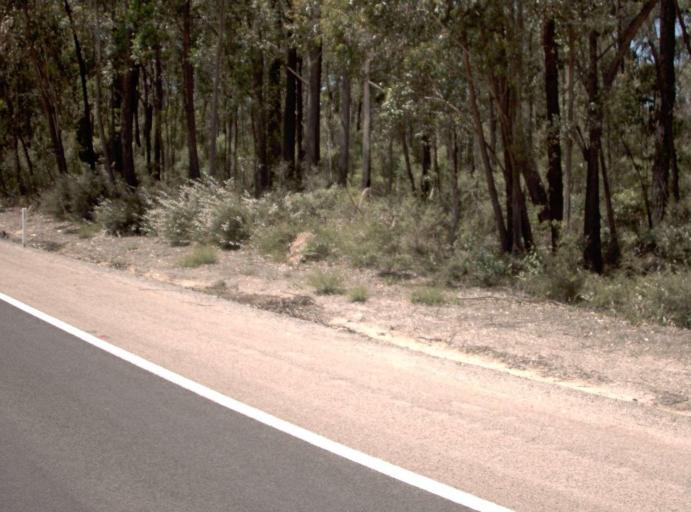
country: AU
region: Victoria
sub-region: East Gippsland
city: Lakes Entrance
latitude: -37.7010
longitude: 148.5853
